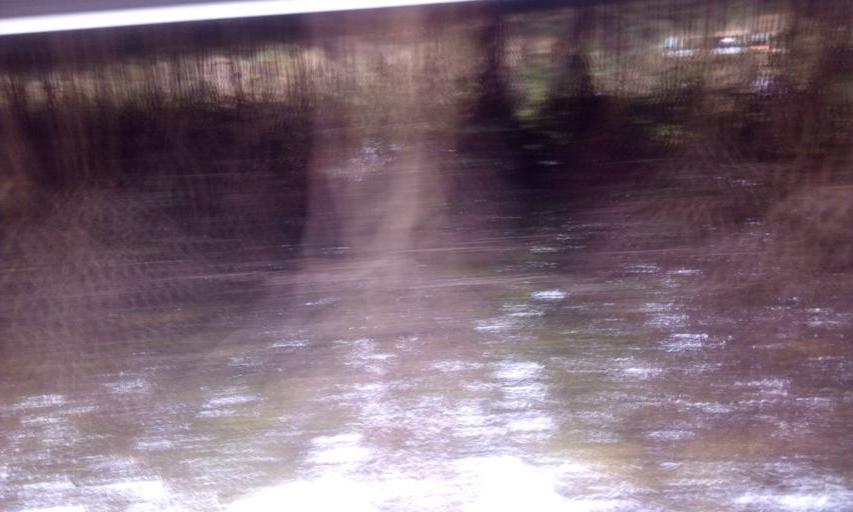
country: TH
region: Trat
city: Laem Ngop
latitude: 12.2084
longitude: 102.2944
